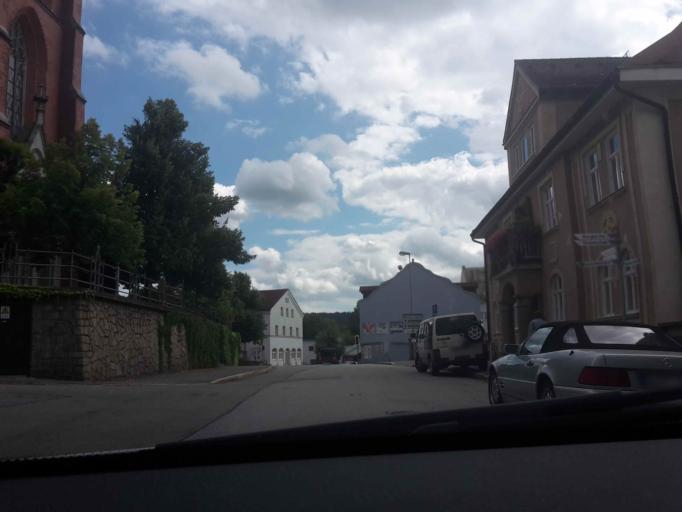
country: DE
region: Bavaria
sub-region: Lower Bavaria
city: Zwiesel
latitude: 49.0153
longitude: 13.2328
